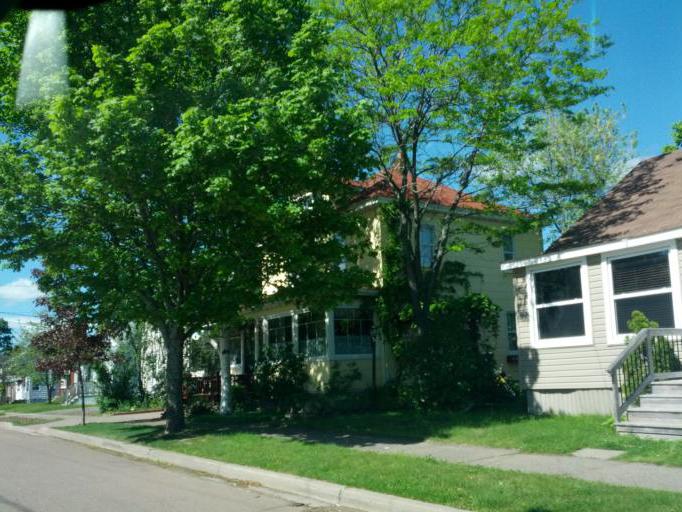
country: CA
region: New Brunswick
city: Moncton
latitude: 46.0985
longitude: -64.7983
